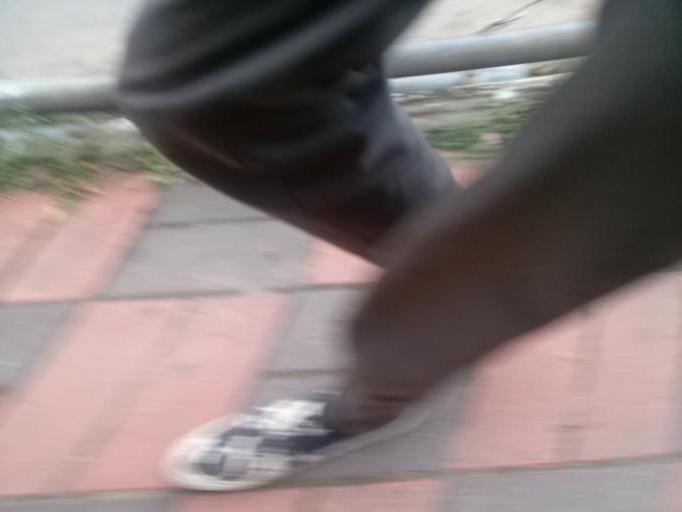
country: IN
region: Kerala
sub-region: Kozhikode
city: Kozhikode
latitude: 11.2554
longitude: 75.7806
